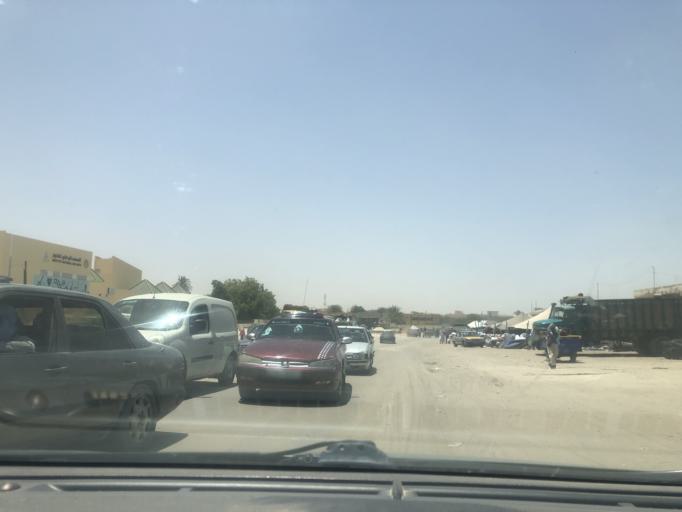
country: MR
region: Nouakchott
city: Nouakchott
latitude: 18.0776
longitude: -15.9822
